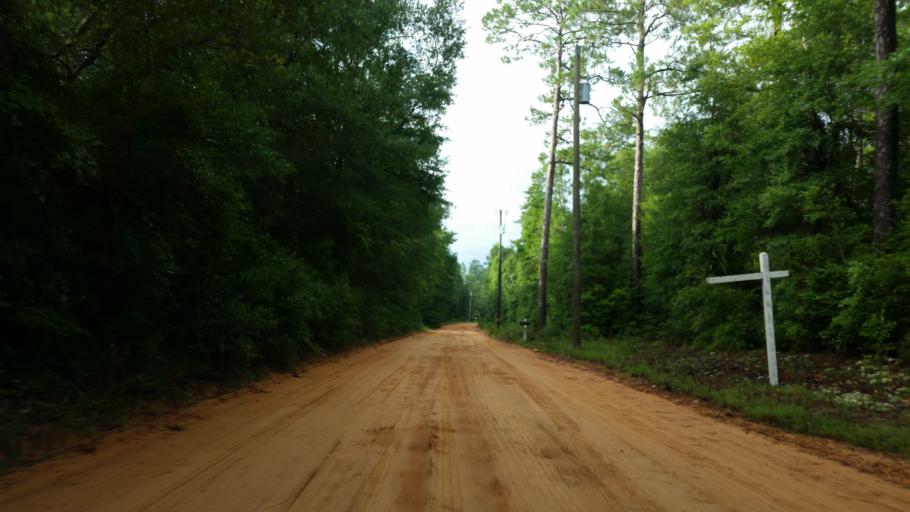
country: US
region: Florida
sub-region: Okaloosa County
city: Crestview
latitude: 30.6721
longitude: -86.7570
